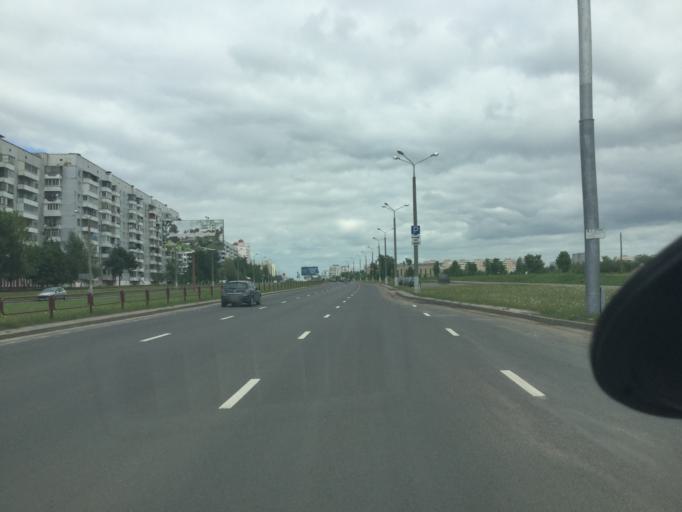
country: BY
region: Vitebsk
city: Vitebsk
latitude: 55.1624
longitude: 30.2222
